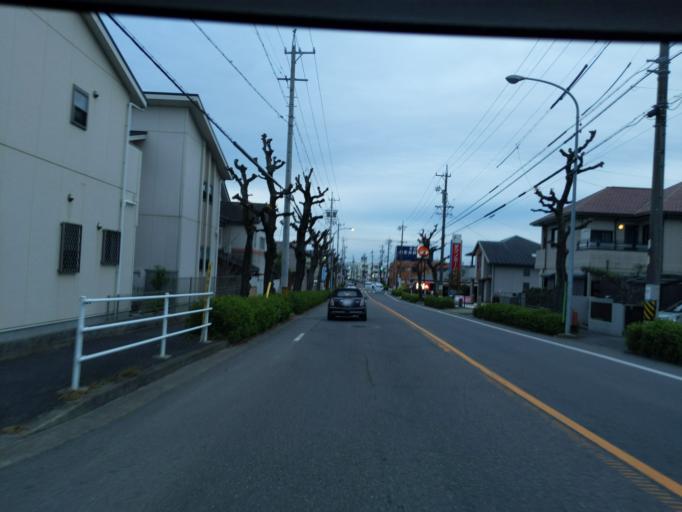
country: JP
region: Aichi
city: Kasugai
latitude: 35.2618
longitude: 136.9732
